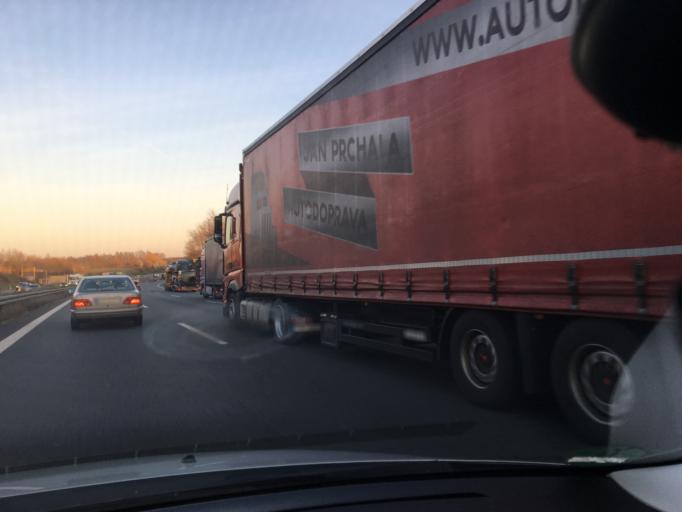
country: DE
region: Baden-Wuerttemberg
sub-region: Karlsruhe Region
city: Ettlingen
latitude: 48.9609
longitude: 8.4742
